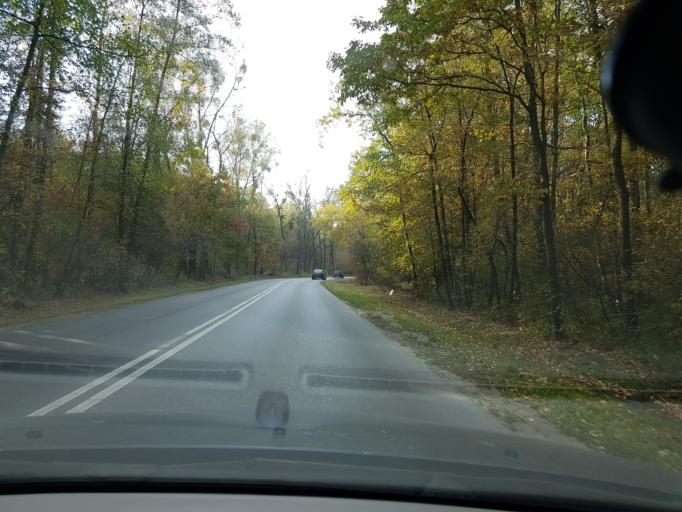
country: PL
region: Masovian Voivodeship
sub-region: Powiat warszawski zachodni
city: Babice
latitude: 52.2739
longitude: 20.8752
